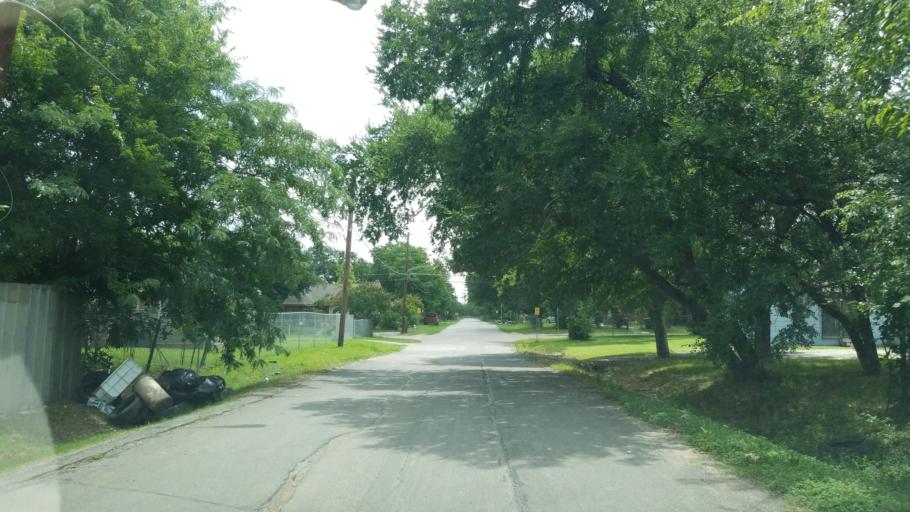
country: US
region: Texas
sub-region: Dallas County
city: Irving
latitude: 32.7887
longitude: -96.9053
